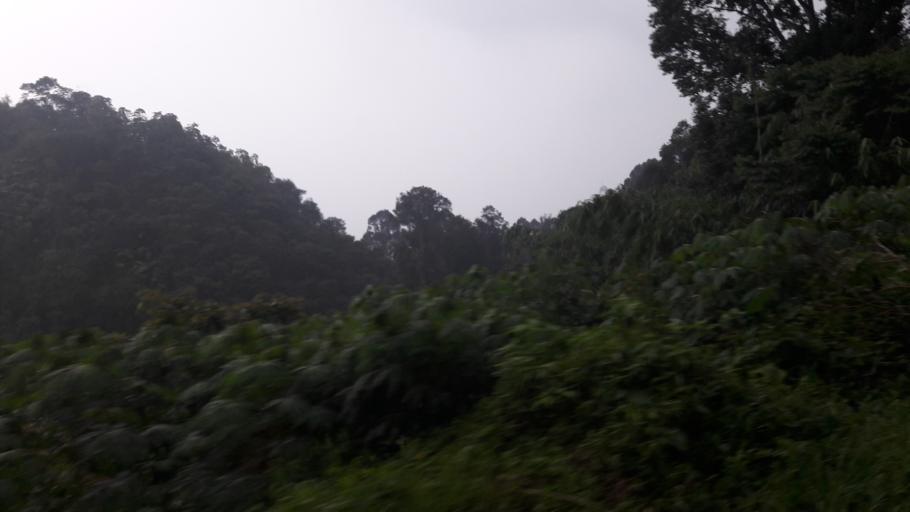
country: ID
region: West Java
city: Cipeundeuy
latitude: -6.6551
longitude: 106.5187
